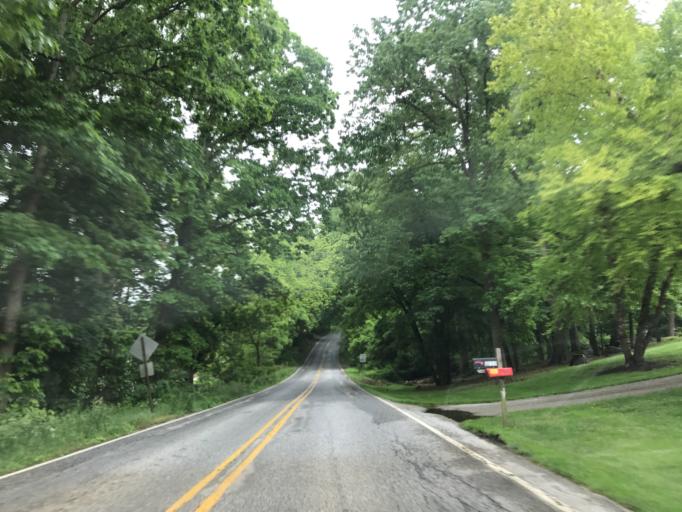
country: US
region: Pennsylvania
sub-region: York County
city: Susquehanna Trails
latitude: 39.7594
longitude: -76.4637
